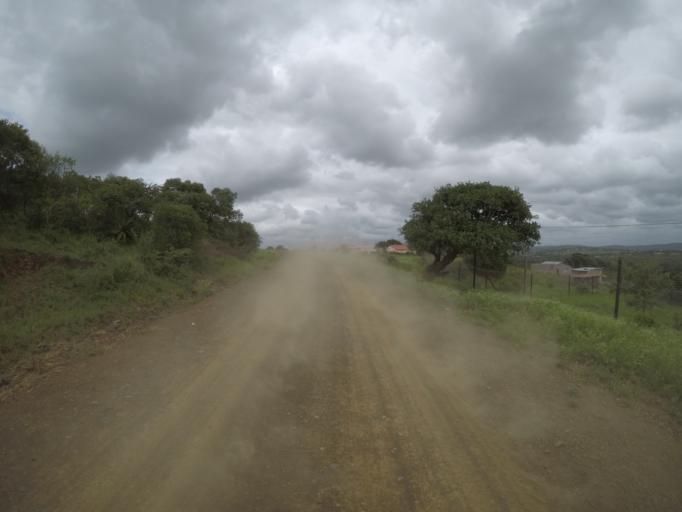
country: ZA
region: KwaZulu-Natal
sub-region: uThungulu District Municipality
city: Empangeni
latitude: -28.5785
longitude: 31.8682
